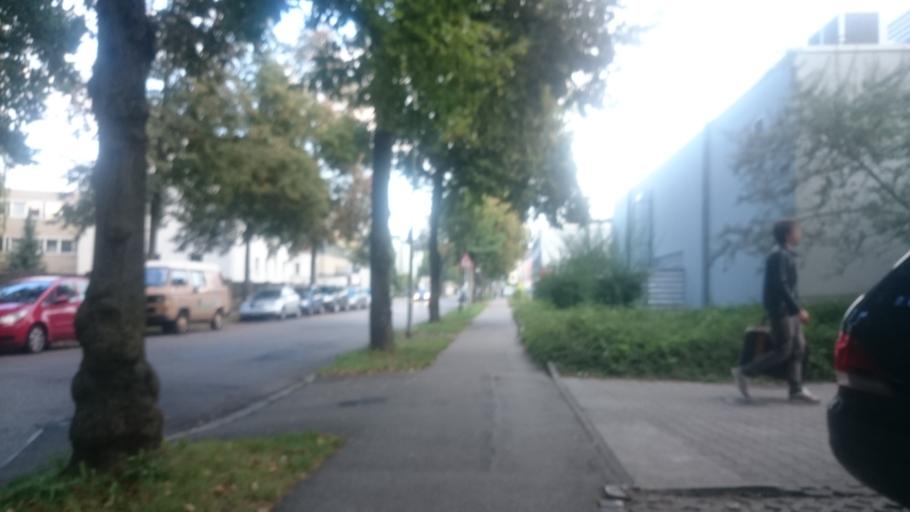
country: DE
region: Bavaria
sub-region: Swabia
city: Augsburg
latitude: 48.3698
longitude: 10.9105
